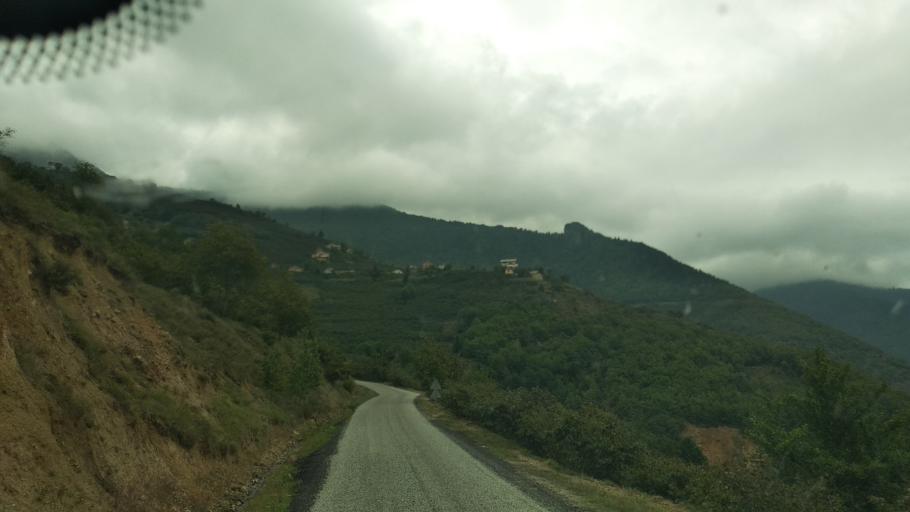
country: TR
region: Giresun
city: Dogankent
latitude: 40.7401
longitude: 38.9904
